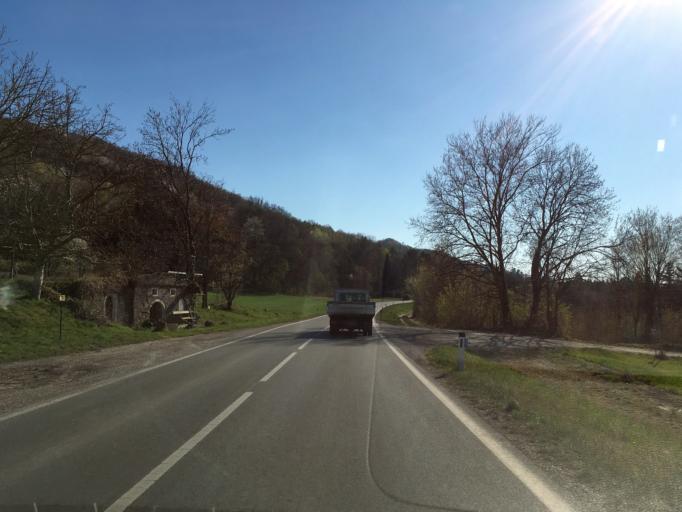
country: AT
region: Lower Austria
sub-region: Politischer Bezirk Tulln
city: Wordern
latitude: 48.3172
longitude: 16.1926
